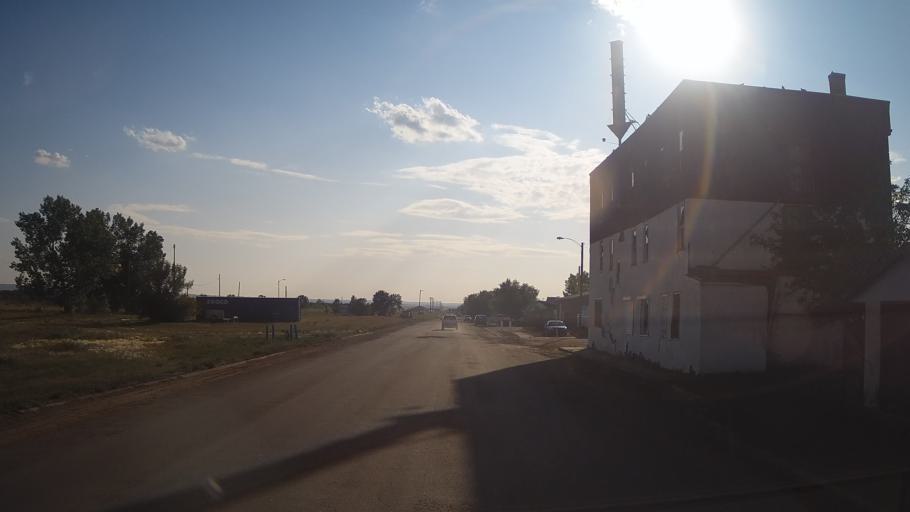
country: CA
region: Alberta
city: Hanna
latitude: 51.6419
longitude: -111.9238
